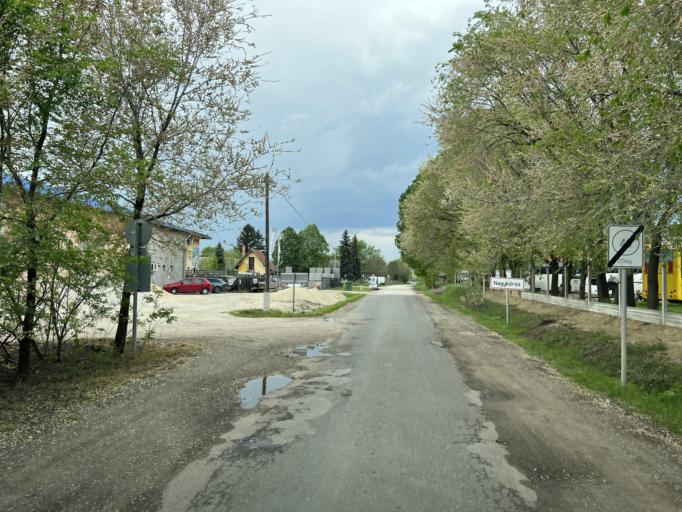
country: HU
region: Pest
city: Nagykoros
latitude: 47.0188
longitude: 19.7919
